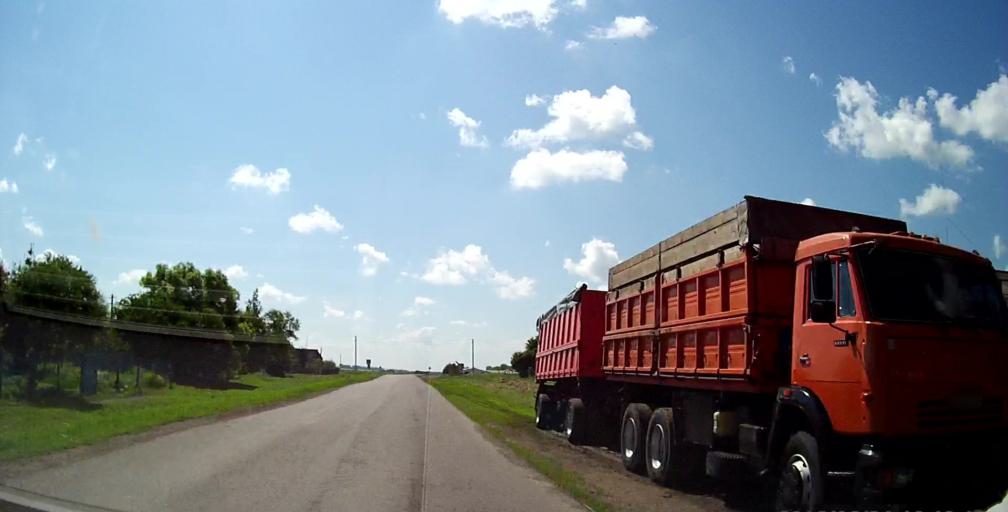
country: RU
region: Lipetsk
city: Chaplygin
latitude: 53.3185
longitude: 39.9583
